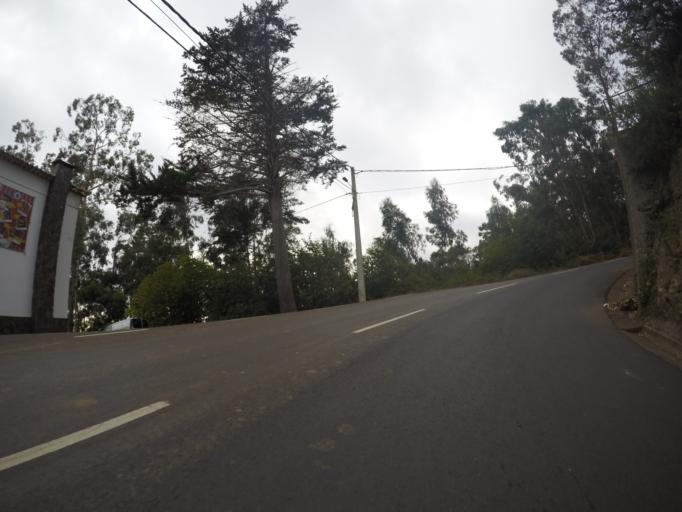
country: PT
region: Madeira
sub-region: Camara de Lobos
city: Curral das Freiras
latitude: 32.6888
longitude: -16.9546
